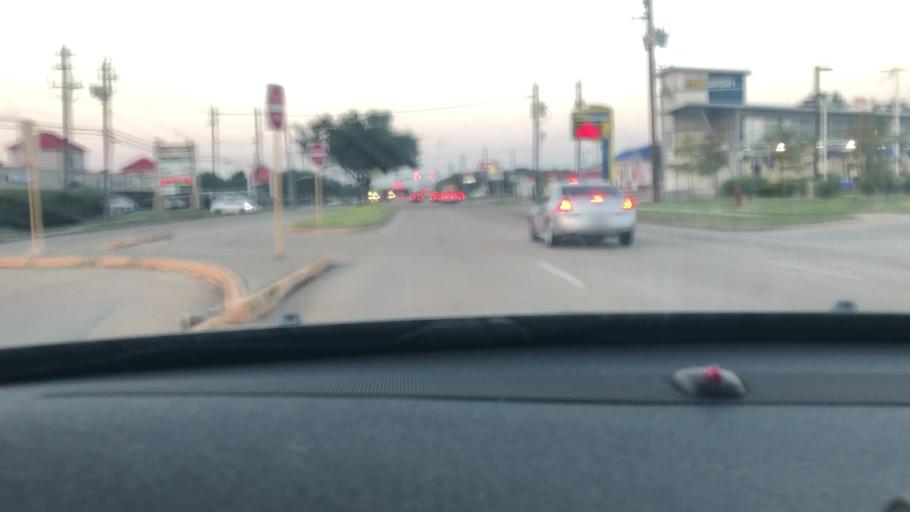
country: US
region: Texas
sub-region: Harris County
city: Webster
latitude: 29.5458
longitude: -95.1327
